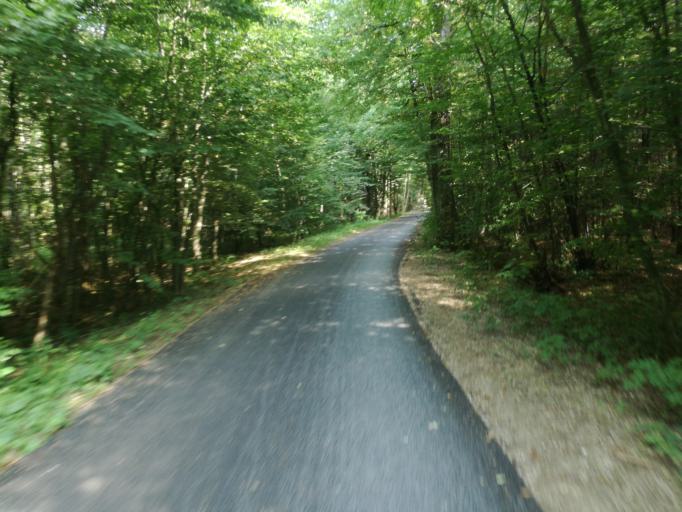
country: DE
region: Bavaria
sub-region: Upper Bavaria
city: Grafelfing
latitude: 48.1270
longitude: 11.4146
